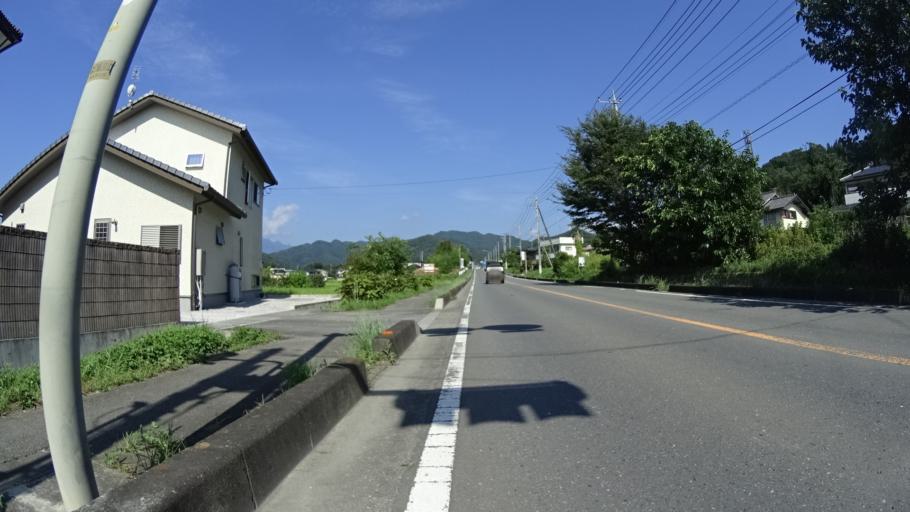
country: JP
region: Saitama
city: Chichibu
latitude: 36.0266
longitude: 138.9955
